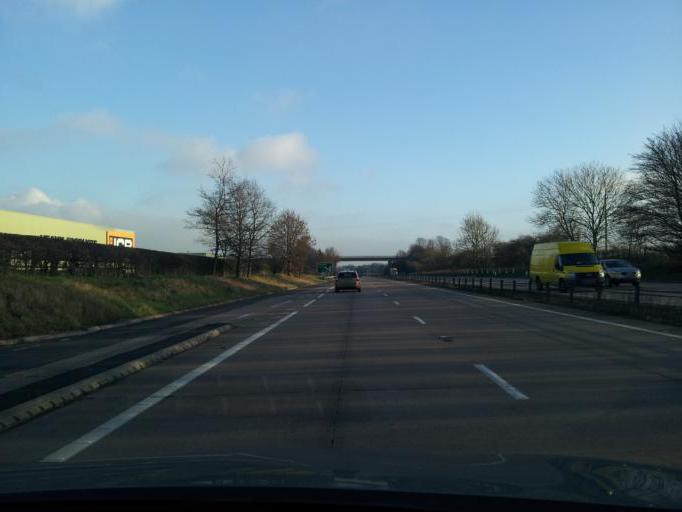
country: GB
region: England
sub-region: Staffordshire
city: Uttoxeter
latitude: 52.9161
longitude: -1.9075
